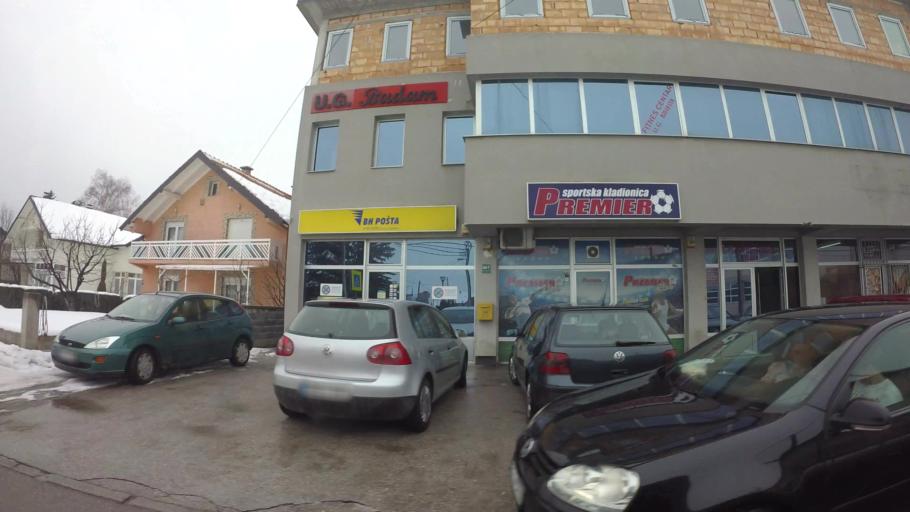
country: BA
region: Federation of Bosnia and Herzegovina
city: Hadzici
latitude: 43.8418
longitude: 18.2771
